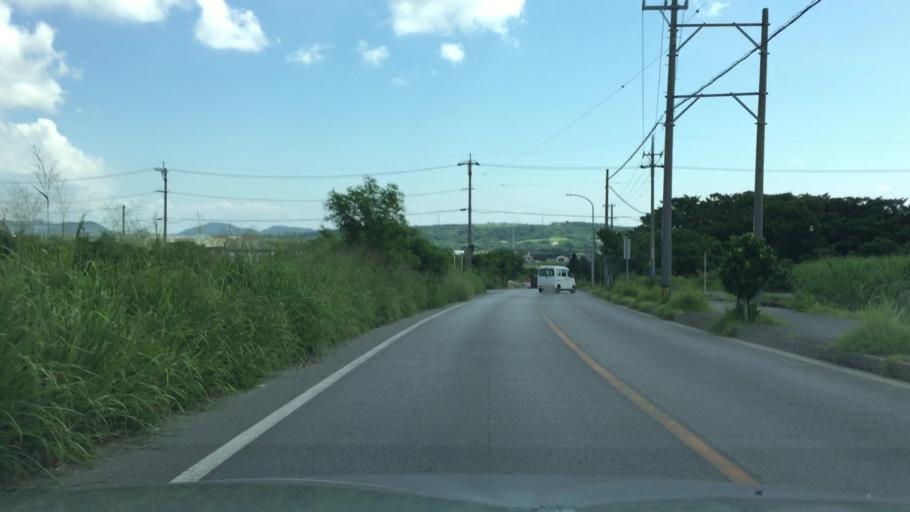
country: JP
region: Okinawa
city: Ishigaki
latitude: 24.3540
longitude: 124.1909
